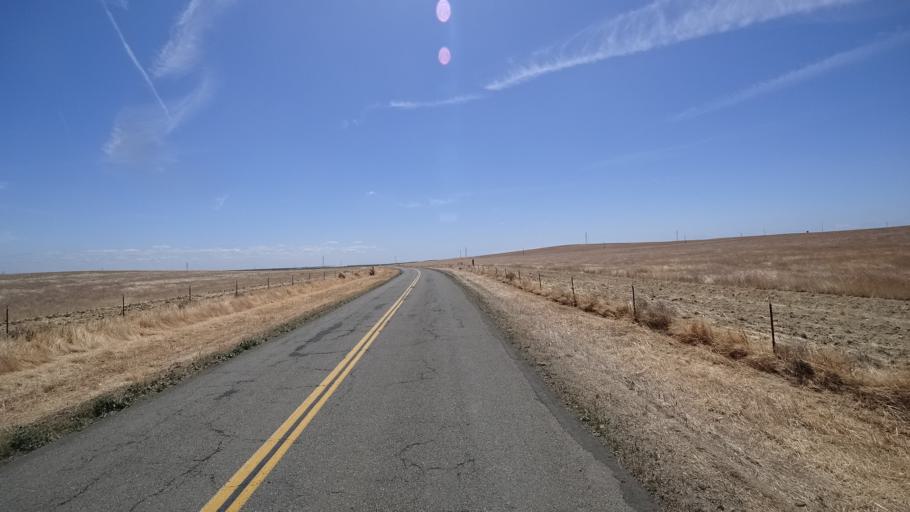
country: US
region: California
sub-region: Kings County
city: Kettleman City
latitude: 35.7948
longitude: -119.8928
